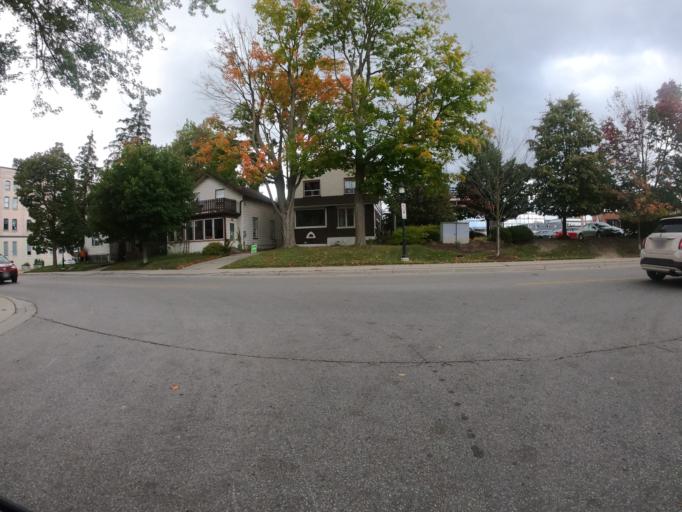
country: CA
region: Ontario
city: Waterloo
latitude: 43.4500
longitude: -80.4970
